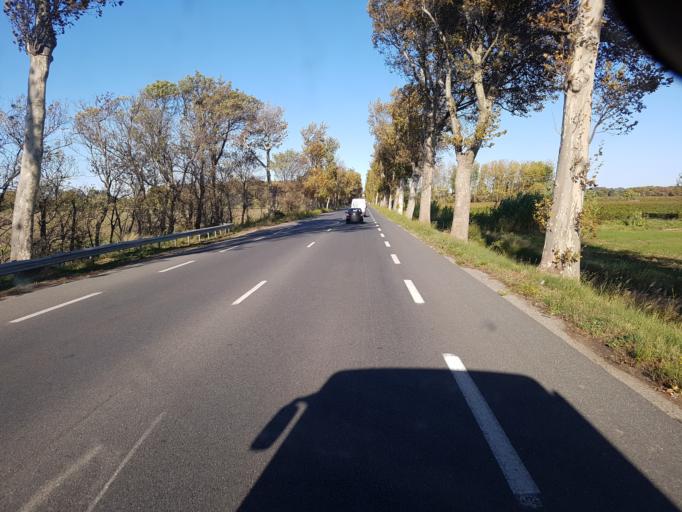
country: FR
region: Languedoc-Roussillon
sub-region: Departement de l'Aude
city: Coursan
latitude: 43.2182
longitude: 3.0372
